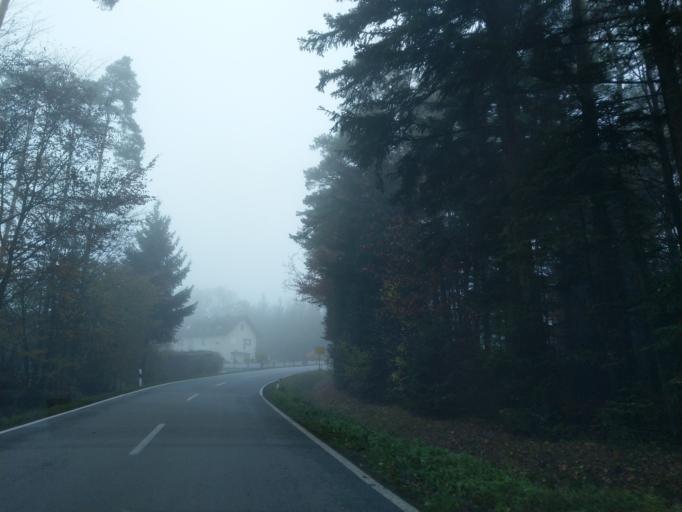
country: DE
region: Bavaria
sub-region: Lower Bavaria
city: Auerbach
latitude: 48.7794
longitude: 13.1081
